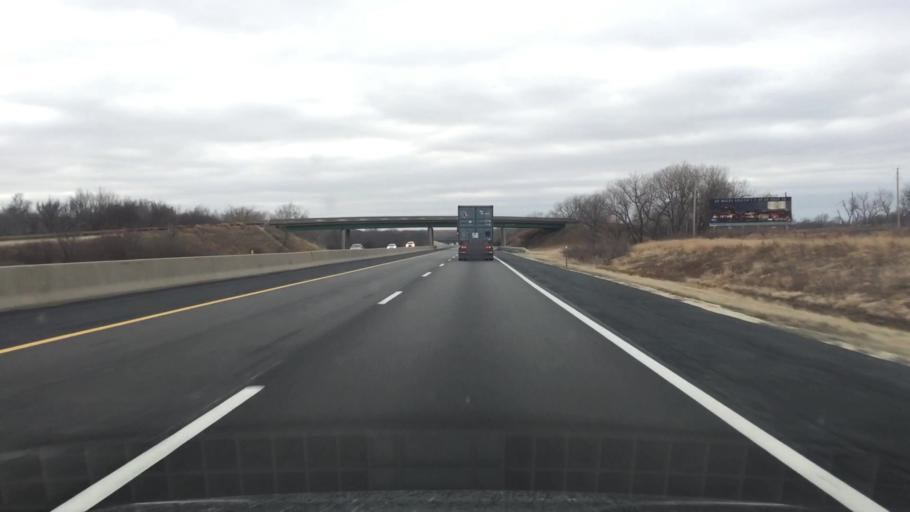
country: US
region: Kansas
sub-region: Chase County
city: Cottonwood Falls
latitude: 38.1457
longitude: -96.5116
